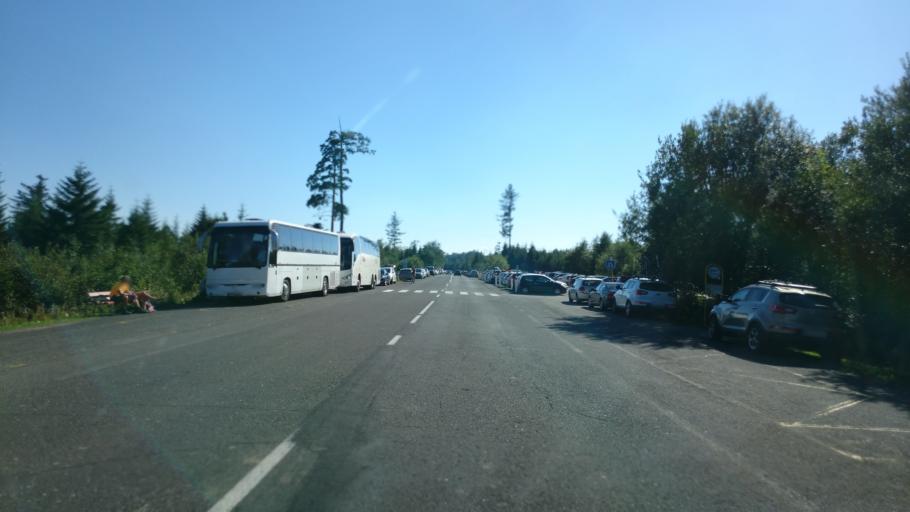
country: SK
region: Presovsky
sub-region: Okres Poprad
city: Nova Lesna
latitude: 49.1882
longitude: 20.2933
